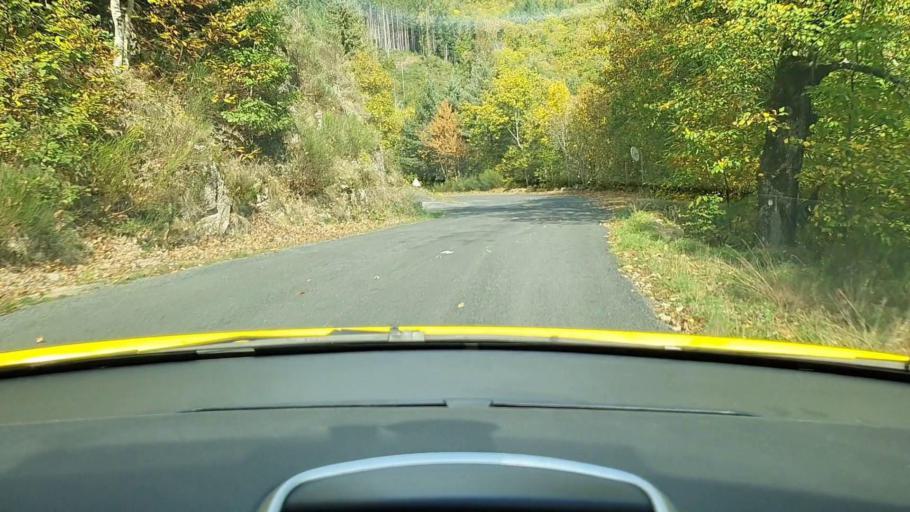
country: FR
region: Languedoc-Roussillon
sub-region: Departement de la Lozere
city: Meyrueis
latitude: 44.0712
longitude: 3.4346
